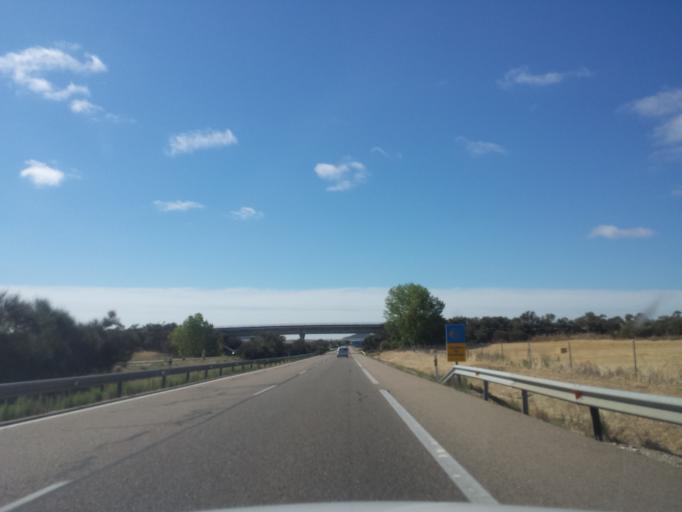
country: ES
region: Castille and Leon
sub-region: Provincia de Valladolid
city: Mota del Marques
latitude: 41.6473
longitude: -5.1898
